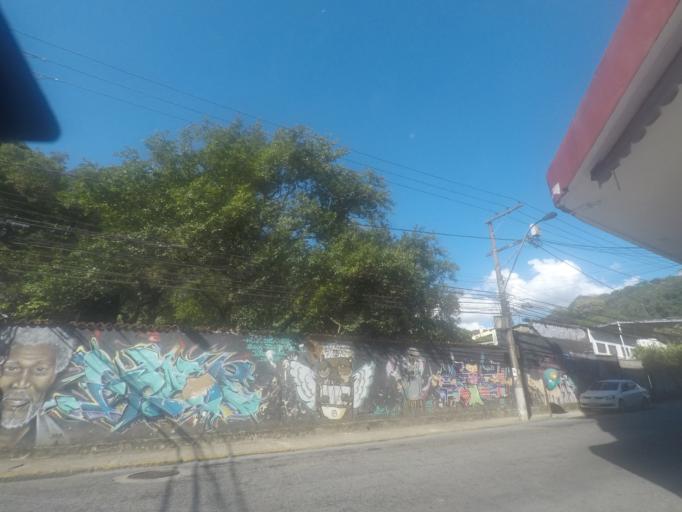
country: BR
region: Rio de Janeiro
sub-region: Petropolis
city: Petropolis
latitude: -22.5346
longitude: -43.1978
